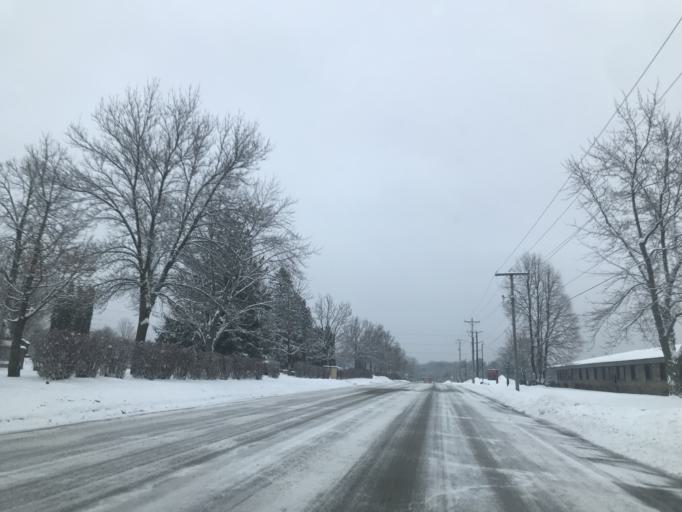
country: US
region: Wisconsin
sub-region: Oconto County
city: Oconto Falls
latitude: 44.8671
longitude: -88.1291
